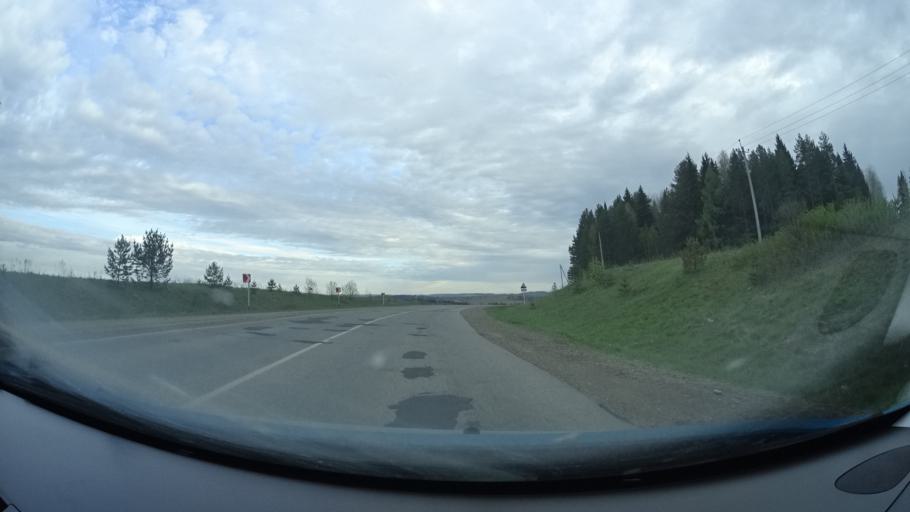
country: RU
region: Perm
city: Osa
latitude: 57.3166
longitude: 55.6230
